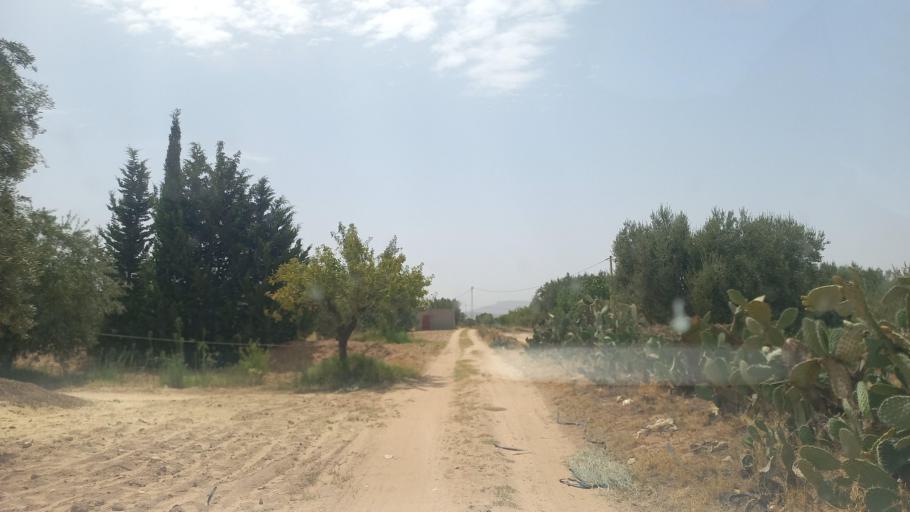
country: TN
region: Al Qasrayn
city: Kasserine
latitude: 35.2630
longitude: 9.0004
